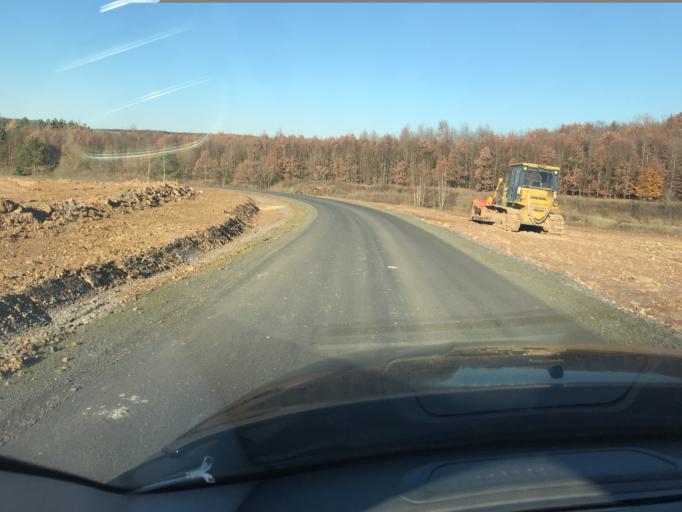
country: DE
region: Rheinland-Pfalz
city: Girod
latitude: 50.4428
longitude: 7.9281
